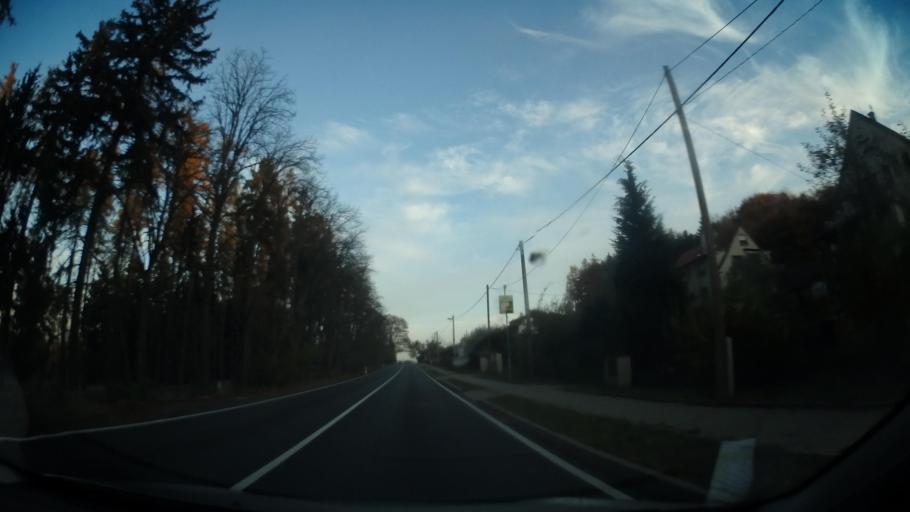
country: CZ
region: Central Bohemia
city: Vlasim
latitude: 49.6878
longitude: 14.9277
